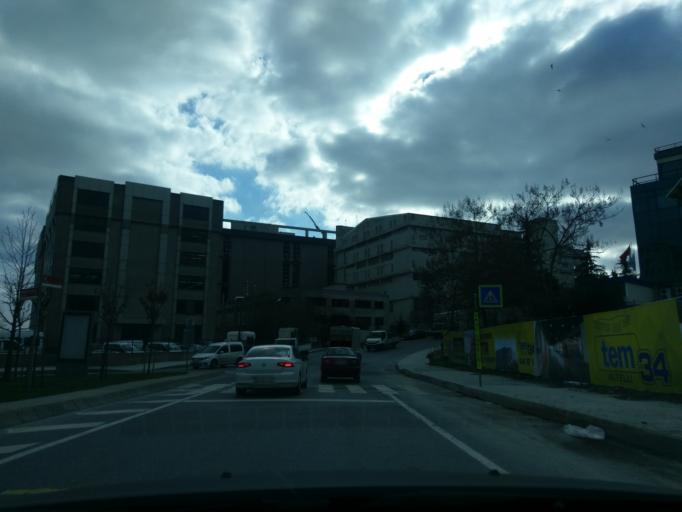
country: TR
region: Istanbul
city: Basaksehir
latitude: 41.0906
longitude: 28.8025
